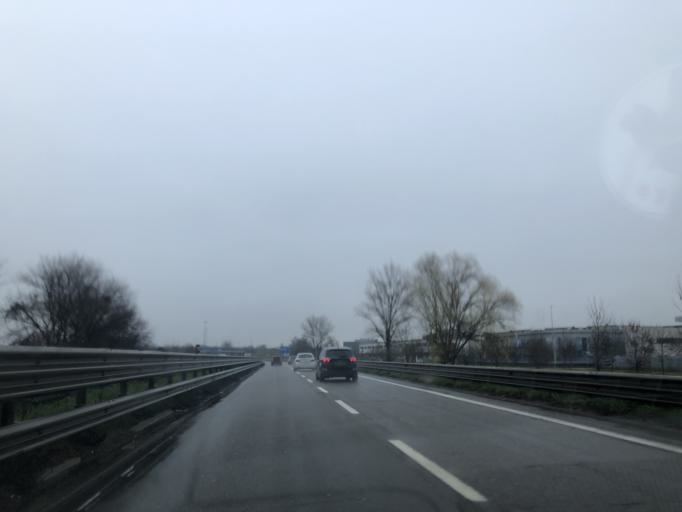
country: IT
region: Emilia-Romagna
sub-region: Provincia di Modena
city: Campogalliano
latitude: 44.6605
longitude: 10.8773
